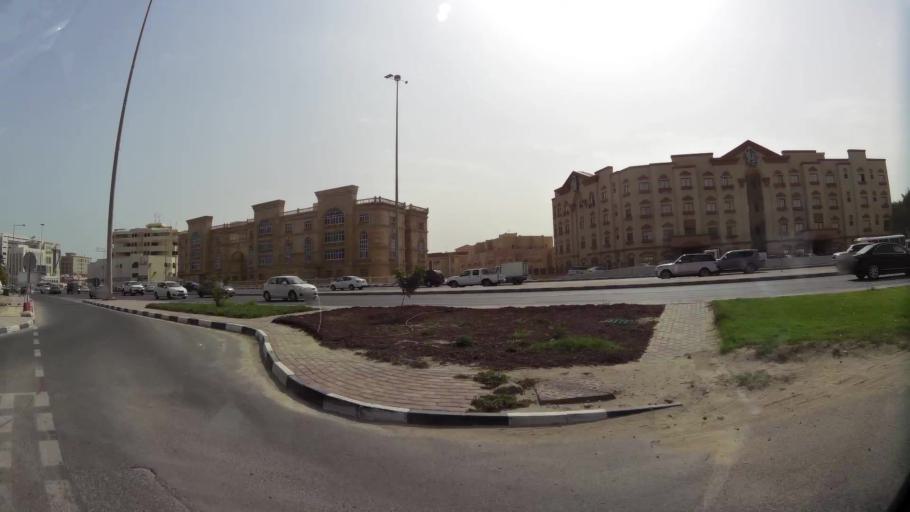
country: QA
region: Baladiyat ad Dawhah
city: Doha
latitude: 25.2788
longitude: 51.4927
